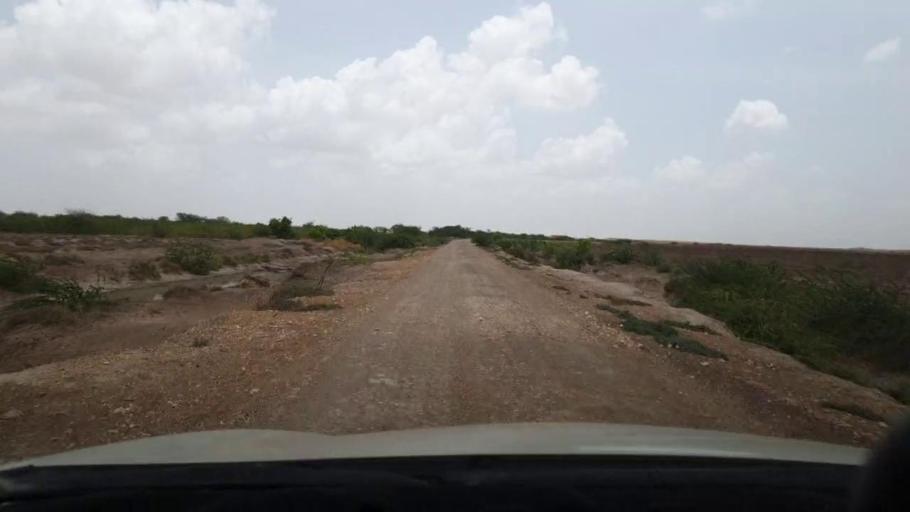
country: PK
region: Sindh
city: Kadhan
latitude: 24.3507
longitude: 68.9235
